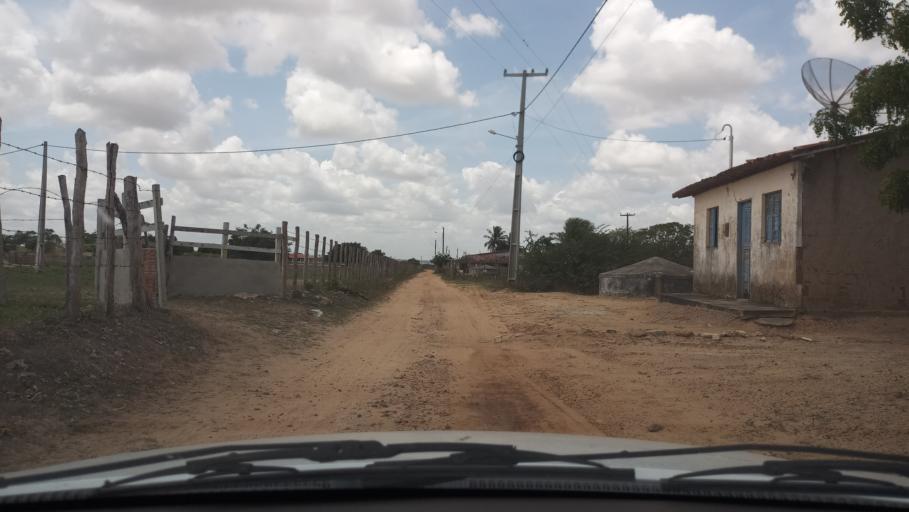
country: BR
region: Rio Grande do Norte
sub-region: Brejinho
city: Brejinho
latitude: -6.2738
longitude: -35.3472
